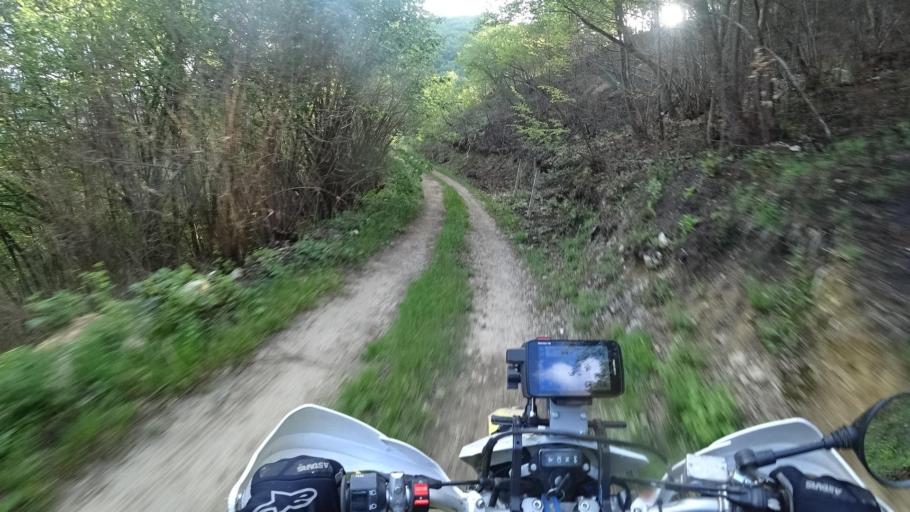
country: BA
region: Federation of Bosnia and Herzegovina
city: Sanica
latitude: 44.6281
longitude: 16.6771
